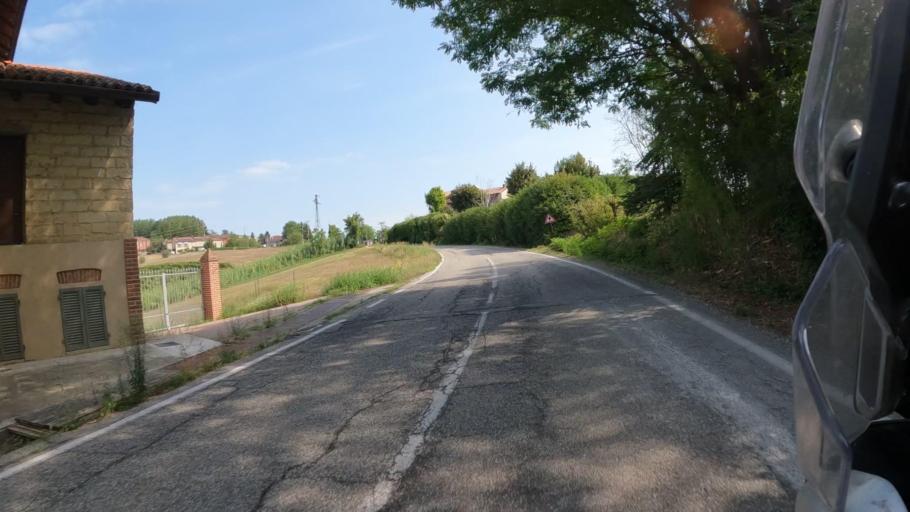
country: IT
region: Piedmont
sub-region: Provincia di Alessandria
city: Rosignano Monferrato
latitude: 45.0814
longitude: 8.4116
